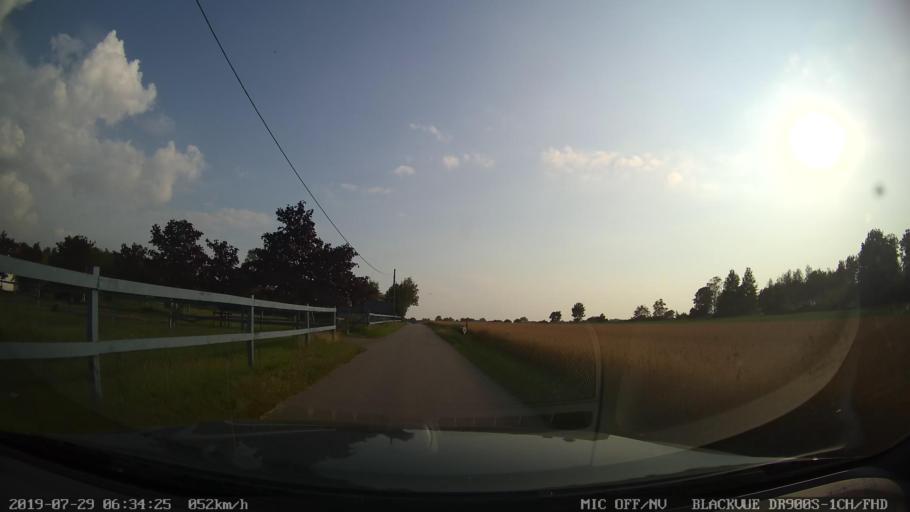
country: SE
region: Skane
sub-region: Helsingborg
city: Odakra
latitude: 56.1207
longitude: 12.7276
